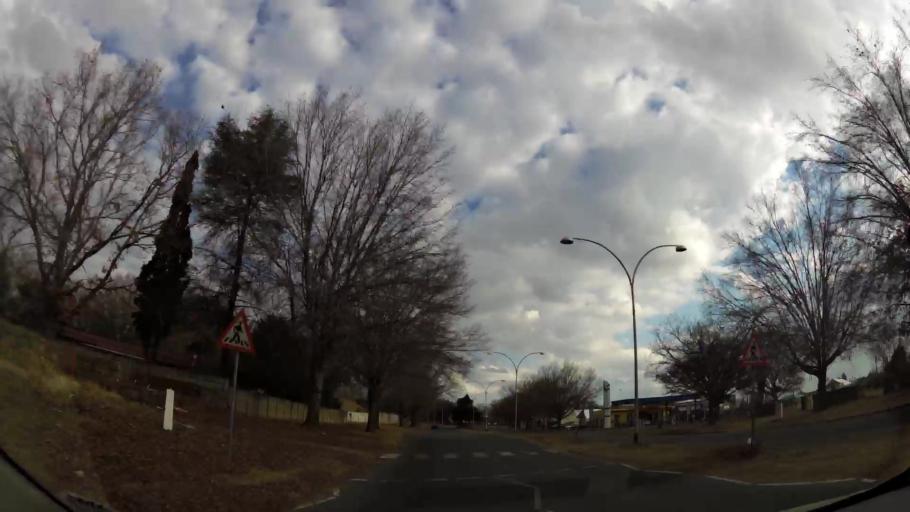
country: ZA
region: Orange Free State
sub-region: Fezile Dabi District Municipality
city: Sasolburg
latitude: -26.8027
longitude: 27.8176
